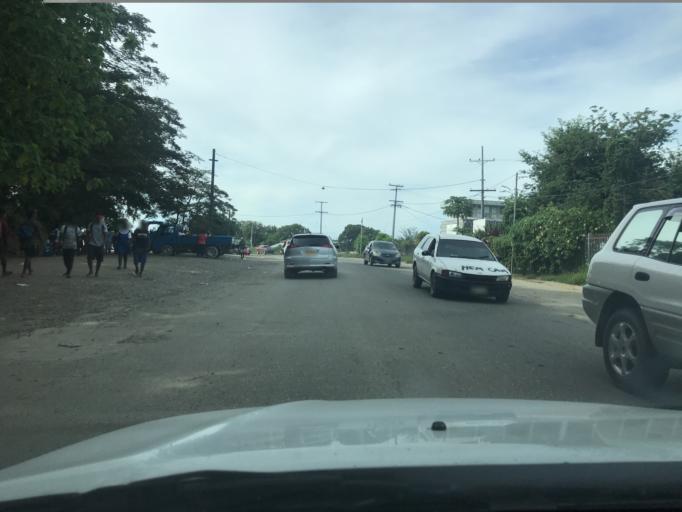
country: SB
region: Guadalcanal
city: Honiara
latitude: -9.4373
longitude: 159.9639
